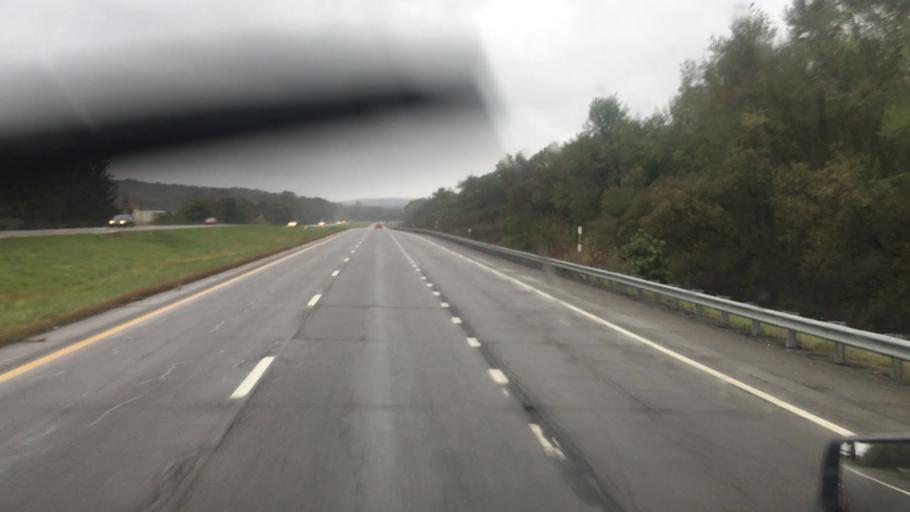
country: US
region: New York
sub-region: Tioga County
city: Apalachin
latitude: 42.0689
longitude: -76.1486
